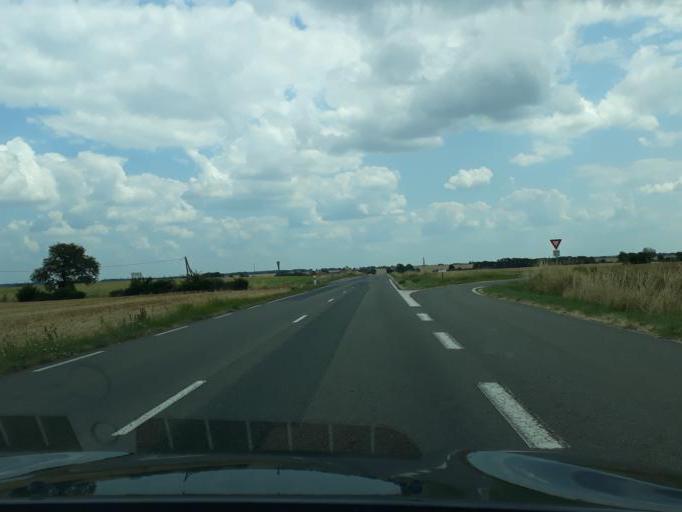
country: FR
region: Centre
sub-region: Departement du Cher
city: Avord
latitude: 47.0194
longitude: 2.6957
